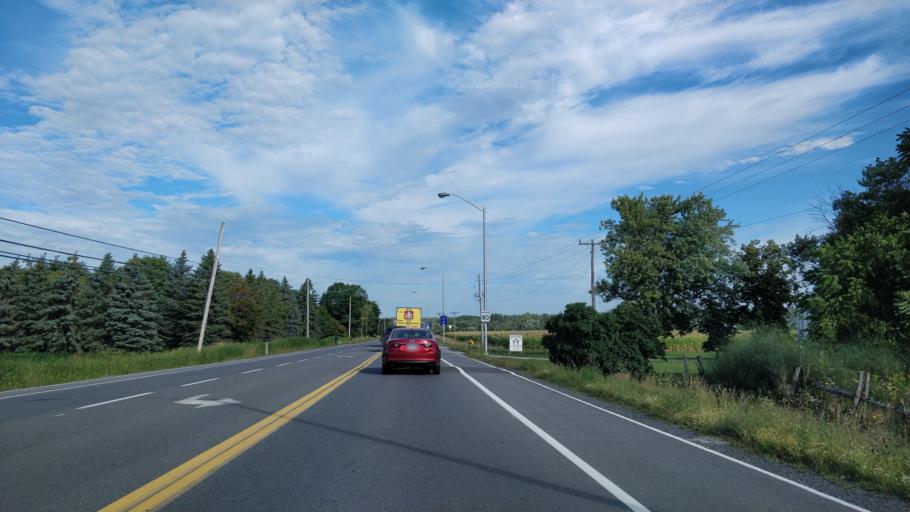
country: CA
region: Ontario
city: Bells Corners
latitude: 45.3350
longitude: -76.0239
